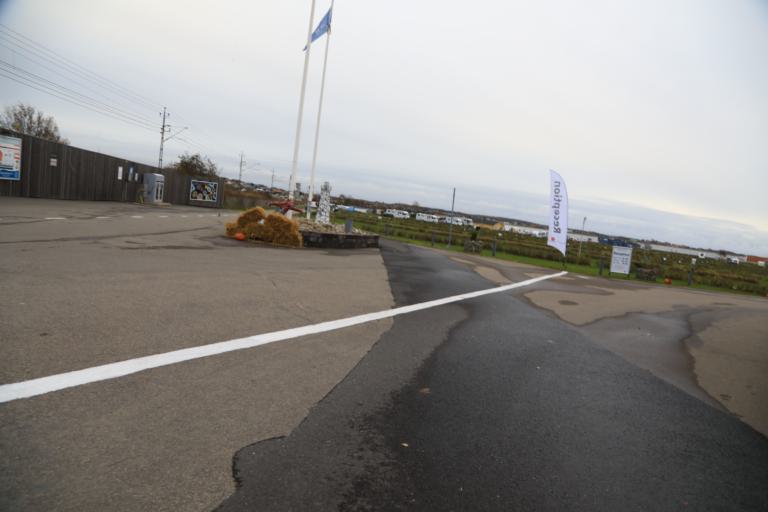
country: SE
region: Halland
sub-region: Varbergs Kommun
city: Varberg
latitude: 57.0880
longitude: 12.2480
